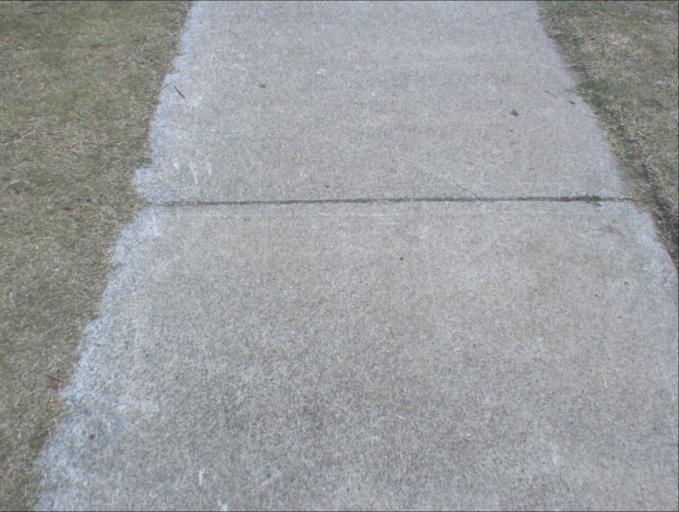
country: AU
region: Queensland
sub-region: Logan
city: Windaroo
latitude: -27.7279
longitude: 153.2090
